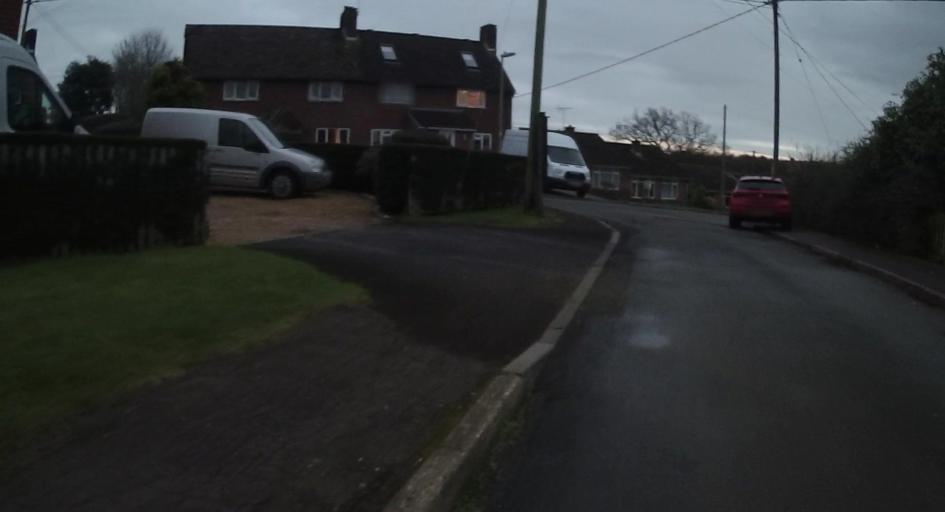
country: GB
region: England
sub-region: Hampshire
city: Four Marks
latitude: 51.0839
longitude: -1.1266
